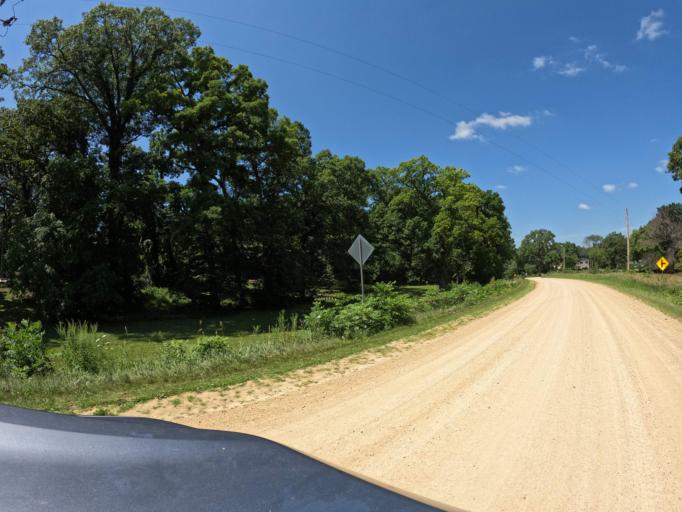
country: US
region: Iowa
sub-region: Clinton County
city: De Witt
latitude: 41.7591
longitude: -90.4312
